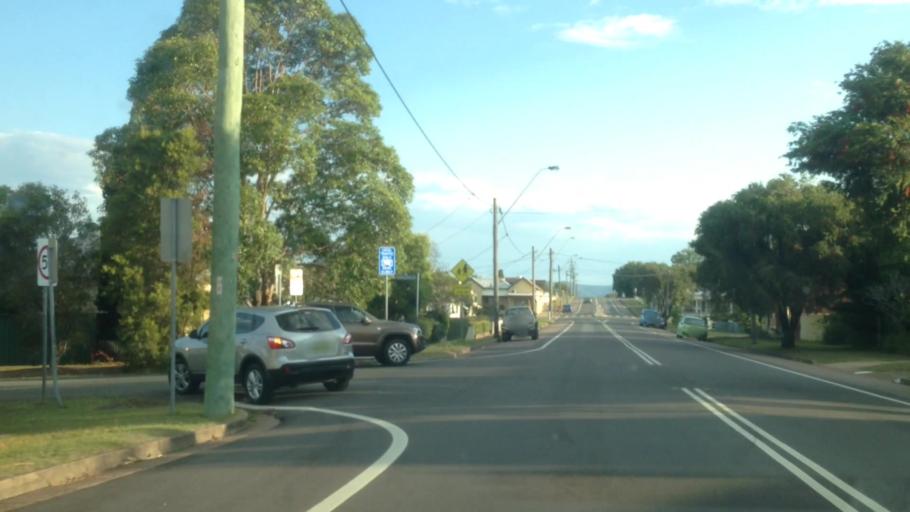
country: AU
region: New South Wales
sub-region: Cessnock
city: Kurri Kurri
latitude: -32.8285
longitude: 151.4815
